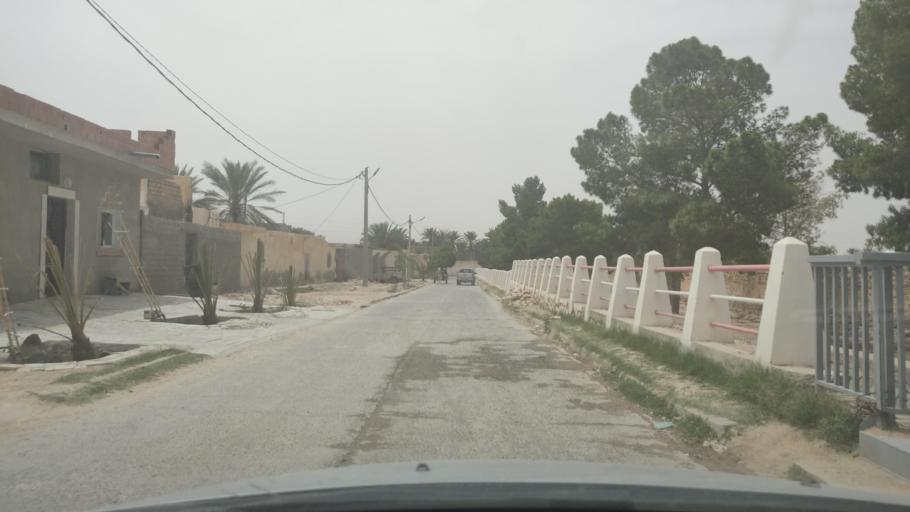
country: TN
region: Gafsa
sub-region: Gafsa Municipality
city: Gafsa
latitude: 34.3327
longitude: 8.9543
